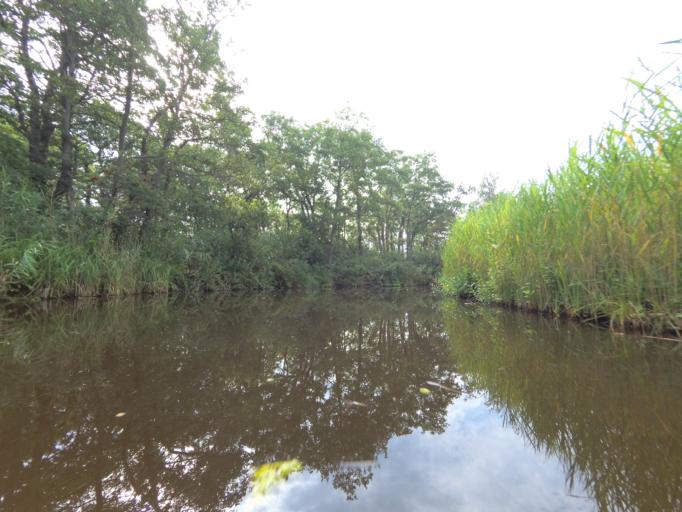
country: NL
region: South Holland
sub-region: Gemeente Nieuwkoop
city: Nieuwkoop
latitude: 52.1536
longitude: 4.8248
